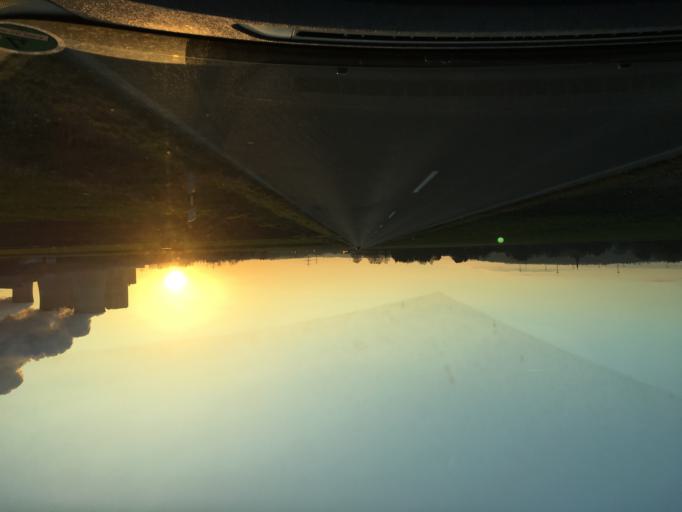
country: DE
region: North Rhine-Westphalia
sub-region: Regierungsbezirk Koln
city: Inden
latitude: 50.8468
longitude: 6.3446
